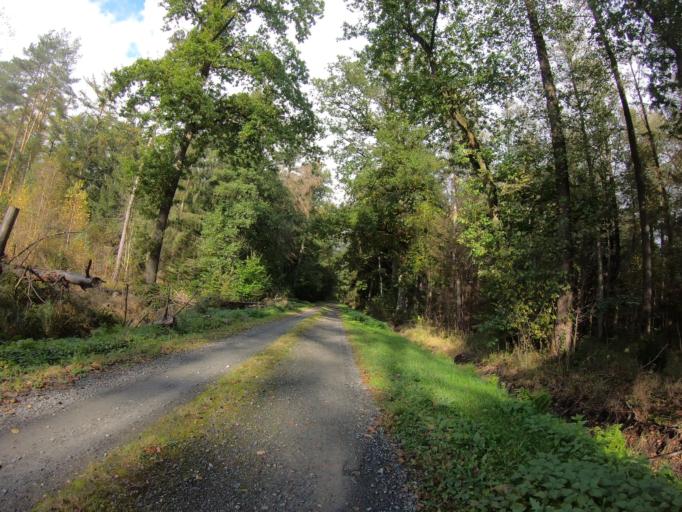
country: DE
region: Lower Saxony
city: Wahrenholz
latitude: 52.5914
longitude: 10.6295
